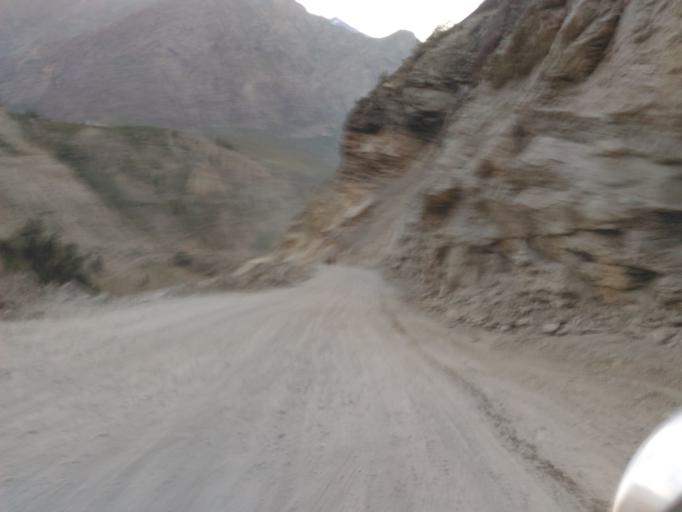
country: IN
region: Himachal Pradesh
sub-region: Lahul and Spiti
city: Kyelang
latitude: 32.5192
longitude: 76.9774
